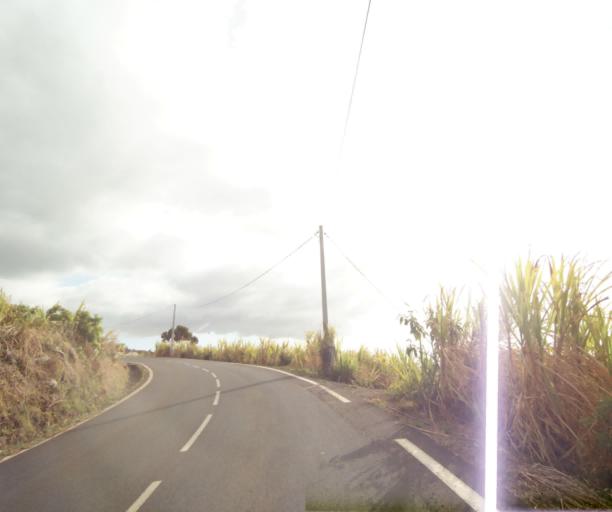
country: RE
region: Reunion
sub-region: Reunion
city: Saint-Paul
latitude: -21.0266
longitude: 55.3124
